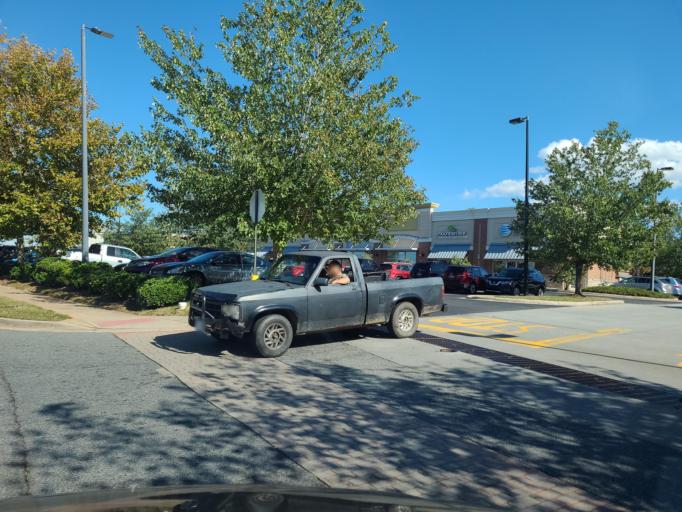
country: US
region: North Carolina
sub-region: Catawba County
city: Conover
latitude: 35.7253
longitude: -81.2106
